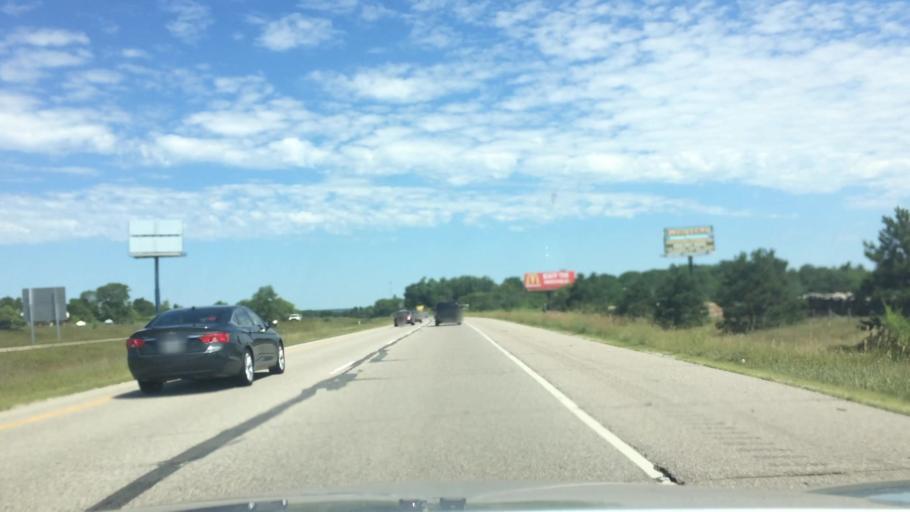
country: US
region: Wisconsin
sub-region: Columbia County
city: Portage
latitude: 43.7088
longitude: -89.4726
